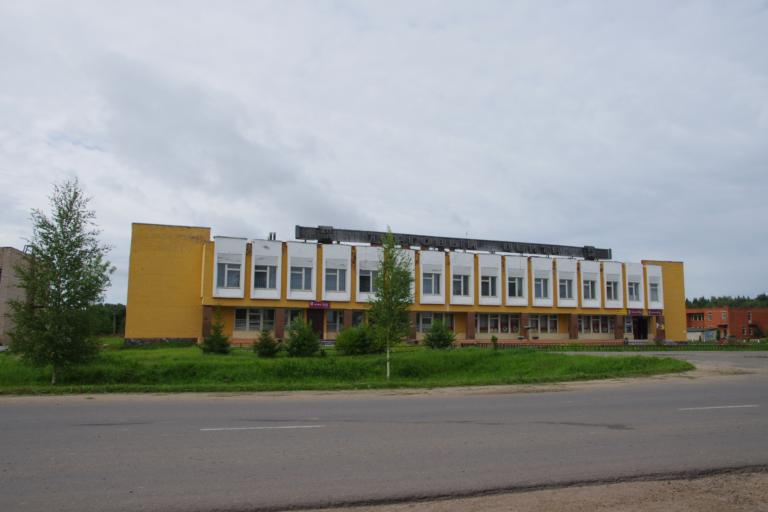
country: BY
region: Vitebsk
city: Chashniki
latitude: 55.3499
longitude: 29.3025
